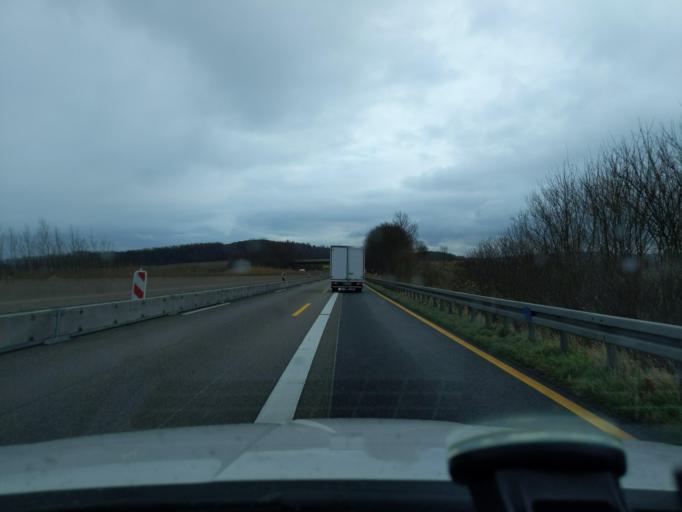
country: DE
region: North Rhine-Westphalia
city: Warburg
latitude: 51.4773
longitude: 9.0764
